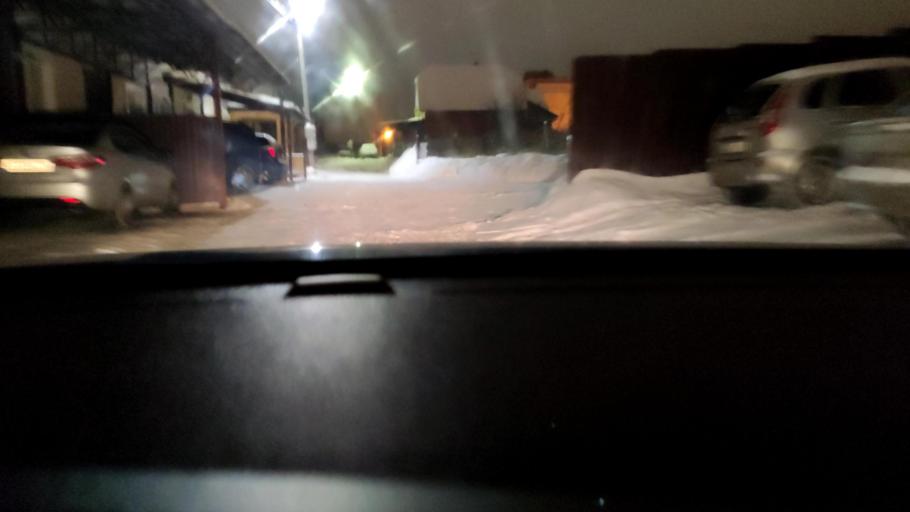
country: RU
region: Tatarstan
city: Vysokaya Gora
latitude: 55.8060
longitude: 49.2641
